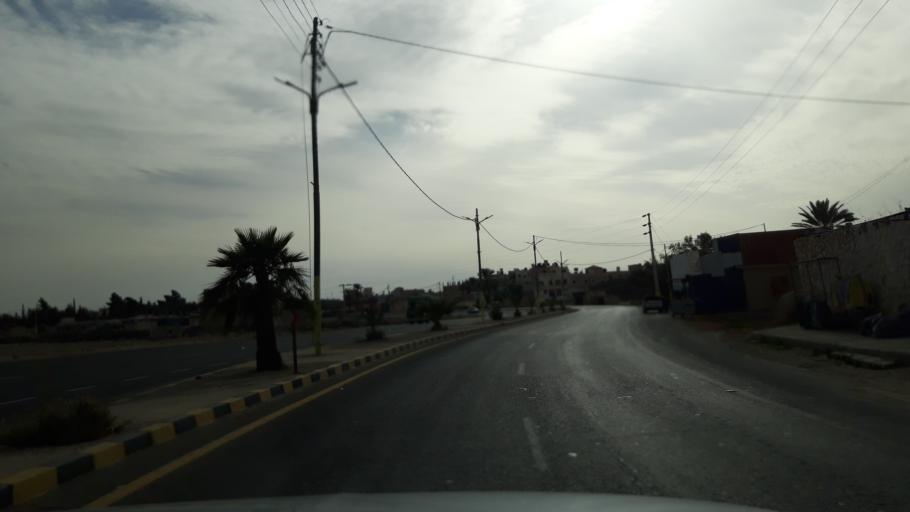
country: JO
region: Amman
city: Al Azraq ash Shamali
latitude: 31.8791
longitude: 36.8270
